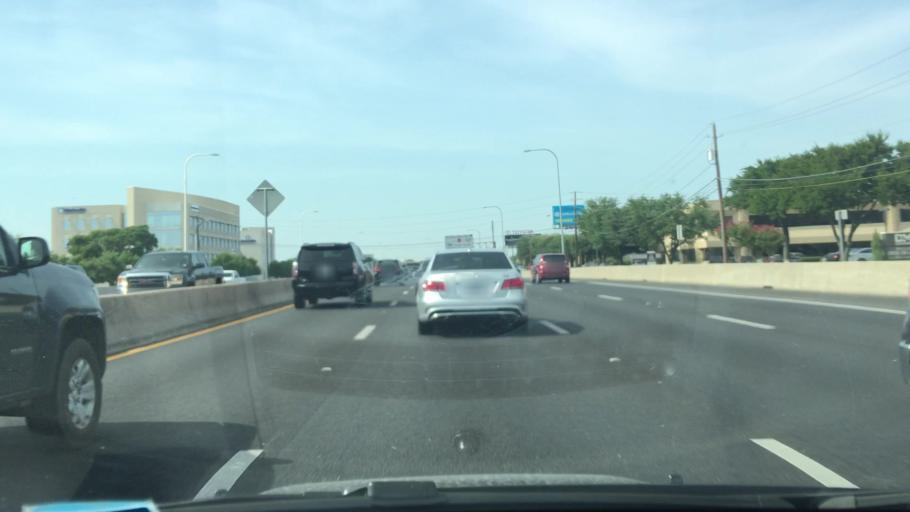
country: US
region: Texas
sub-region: Dallas County
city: Addison
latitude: 32.9818
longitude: -96.8287
